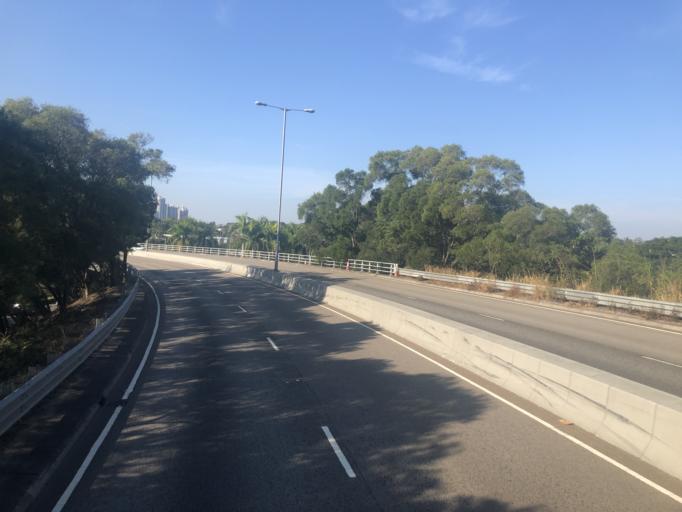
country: HK
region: Yuen Long
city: Yuen Long Kau Hui
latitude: 22.4459
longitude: 114.0164
